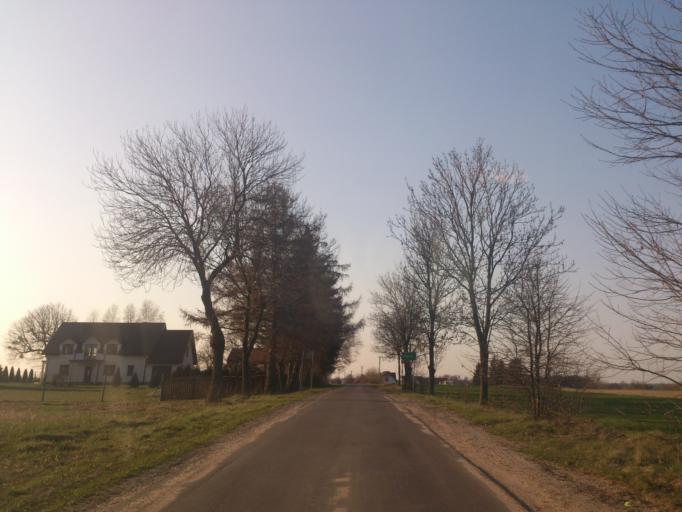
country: PL
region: Kujawsko-Pomorskie
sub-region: Powiat golubsko-dobrzynski
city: Radomin
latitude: 53.1189
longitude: 19.1390
